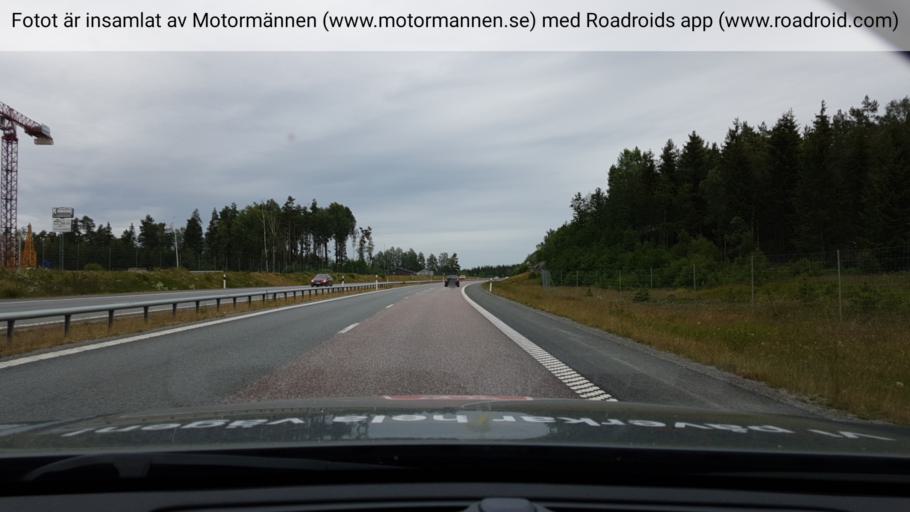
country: SE
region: Stockholm
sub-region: Haninge Kommun
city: Jordbro
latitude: 59.0832
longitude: 18.0804
